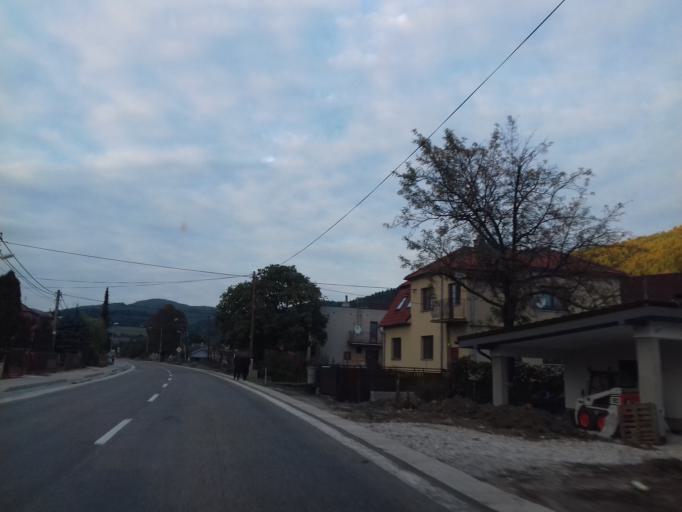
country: SK
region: Trenciansky
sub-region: Okres Trencin
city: Trencin
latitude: 48.9002
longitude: 17.9525
